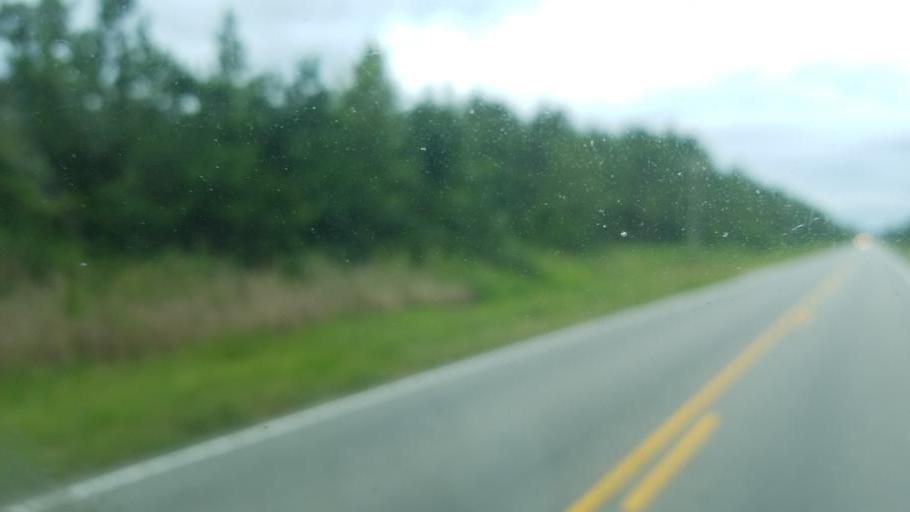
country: US
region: North Carolina
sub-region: Tyrrell County
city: Columbia
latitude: 35.9336
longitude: -76.1657
